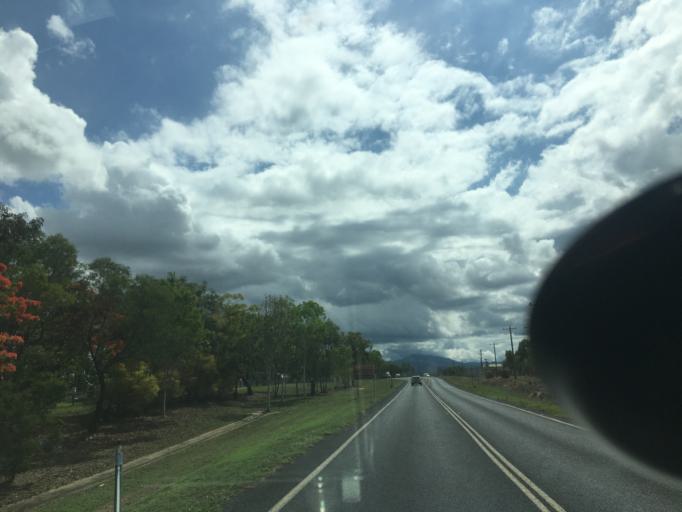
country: AU
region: Queensland
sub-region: Tablelands
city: Mareeba
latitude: -17.0046
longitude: 145.4458
